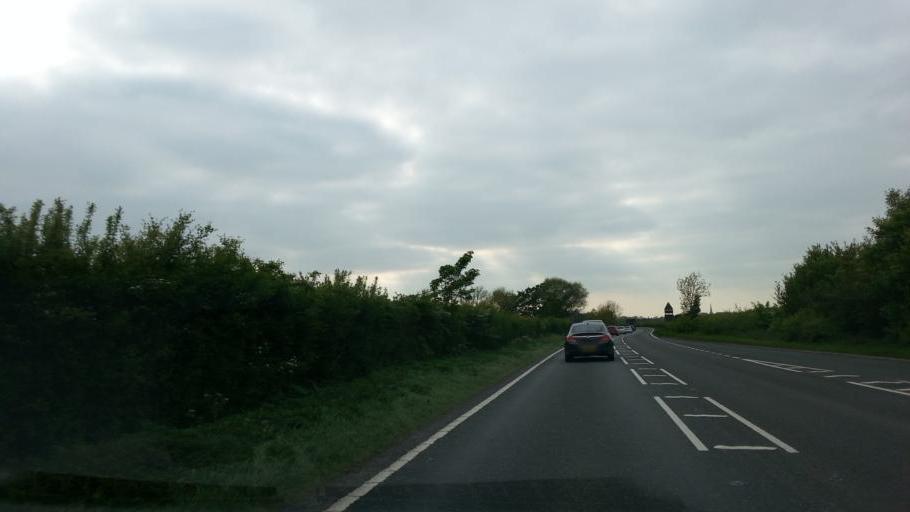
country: GB
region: England
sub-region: Lincolnshire
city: Navenby
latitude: 53.0631
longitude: -0.6063
